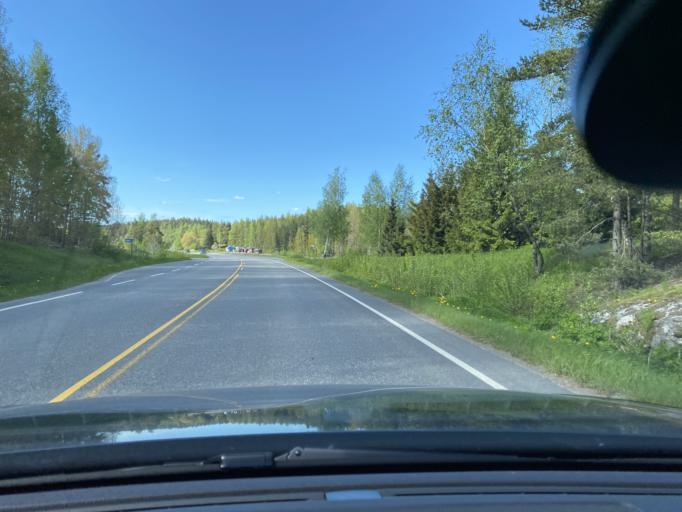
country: FI
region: Varsinais-Suomi
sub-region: Turku
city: Sauvo
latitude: 60.3676
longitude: 22.6742
